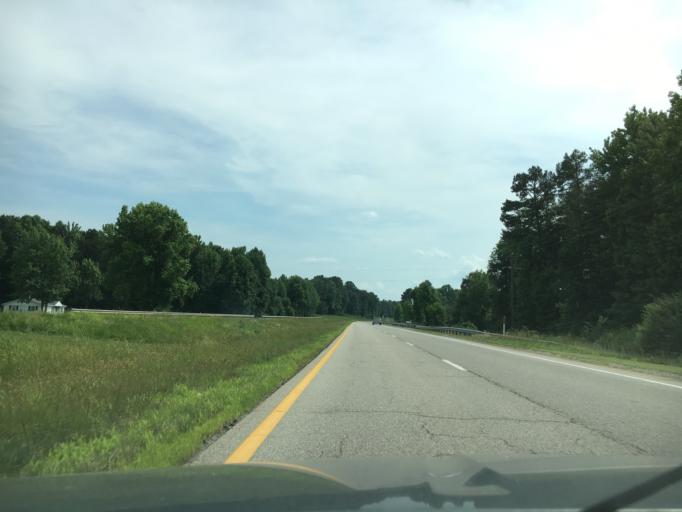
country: US
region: Virginia
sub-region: Nottoway County
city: Crewe
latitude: 37.1761
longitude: -78.2452
